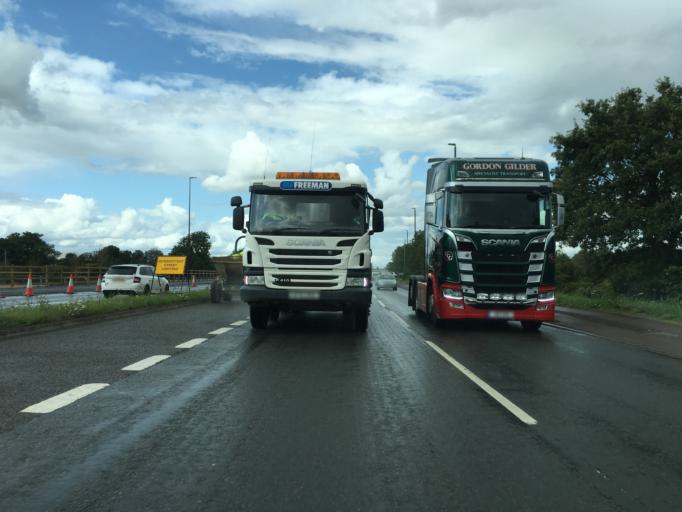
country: GB
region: England
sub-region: Gloucestershire
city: Stonehouse
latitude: 51.8031
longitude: -2.2894
